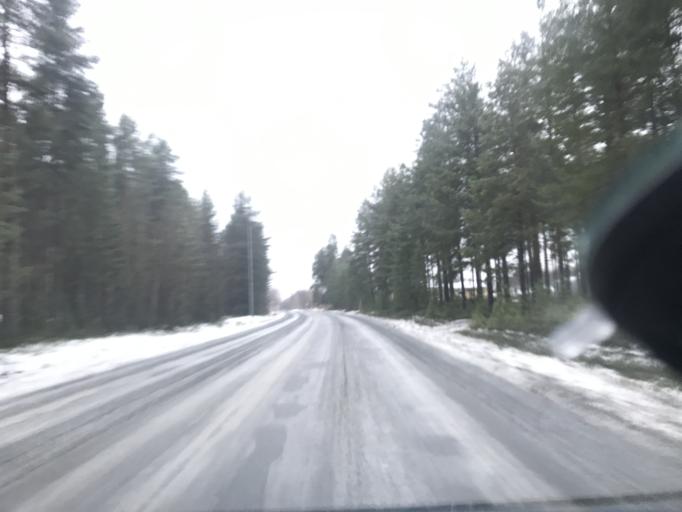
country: SE
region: Norrbotten
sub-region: Lulea Kommun
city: Sodra Sunderbyn
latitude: 65.6515
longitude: 21.9538
